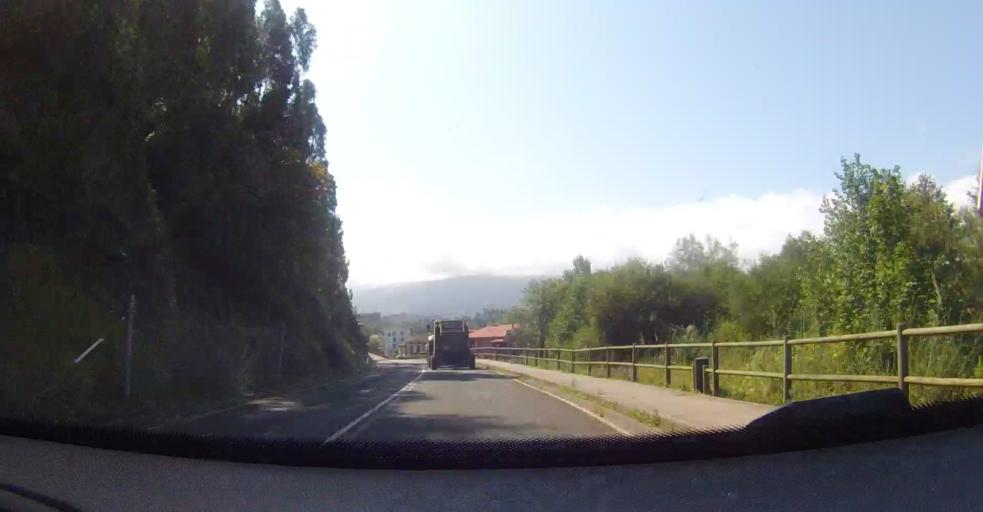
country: ES
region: Asturias
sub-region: Province of Asturias
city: Colunga
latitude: 43.4867
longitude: -5.2759
